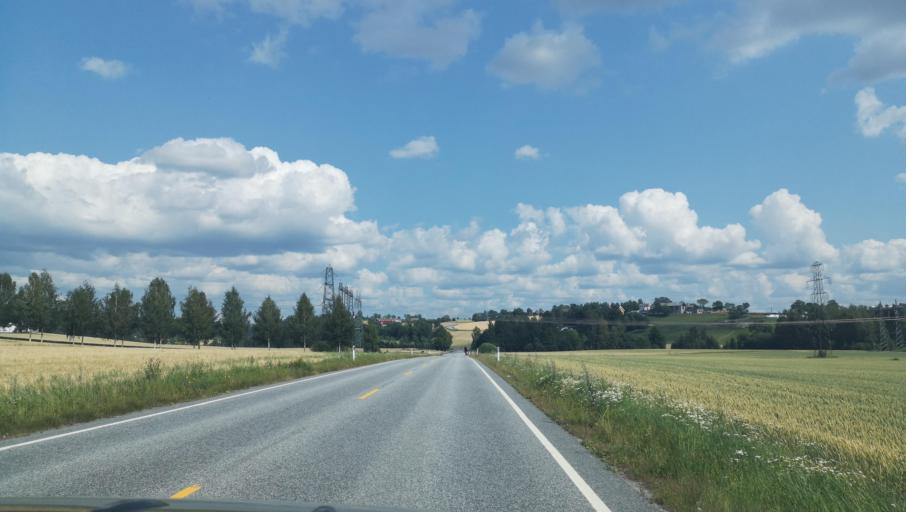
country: NO
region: Buskerud
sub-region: Ovre Eiker
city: Hokksund
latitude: 59.7218
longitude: 9.8288
